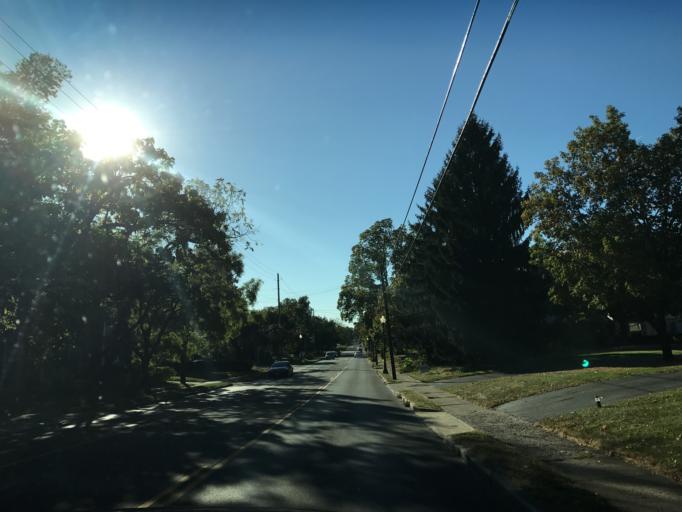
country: US
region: Ohio
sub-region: Franklin County
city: Worthington
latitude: 40.0886
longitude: -83.0101
